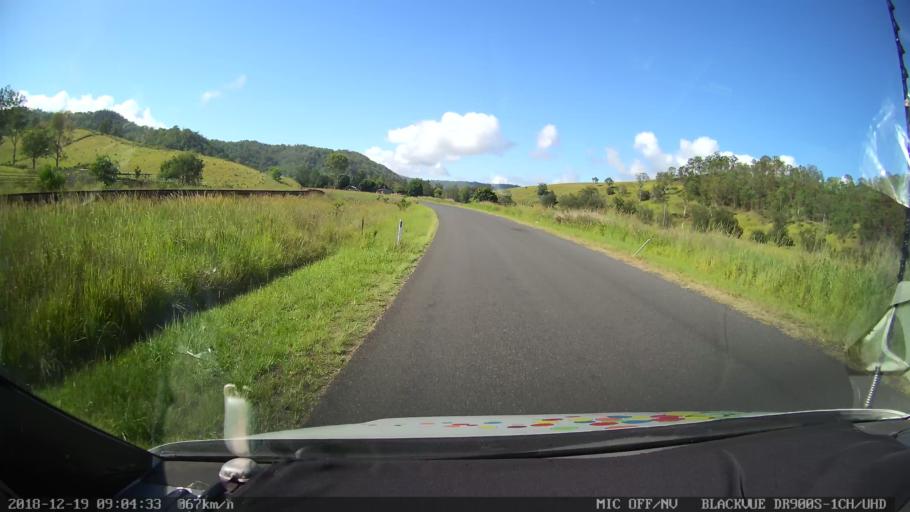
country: AU
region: New South Wales
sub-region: Kyogle
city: Kyogle
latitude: -28.4557
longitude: 152.9444
